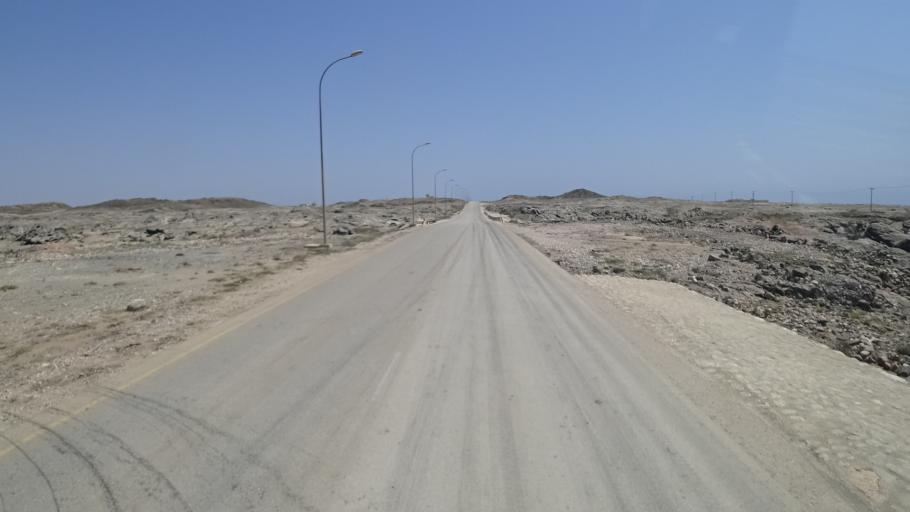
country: OM
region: Zufar
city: Salalah
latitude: 16.9714
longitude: 54.7218
